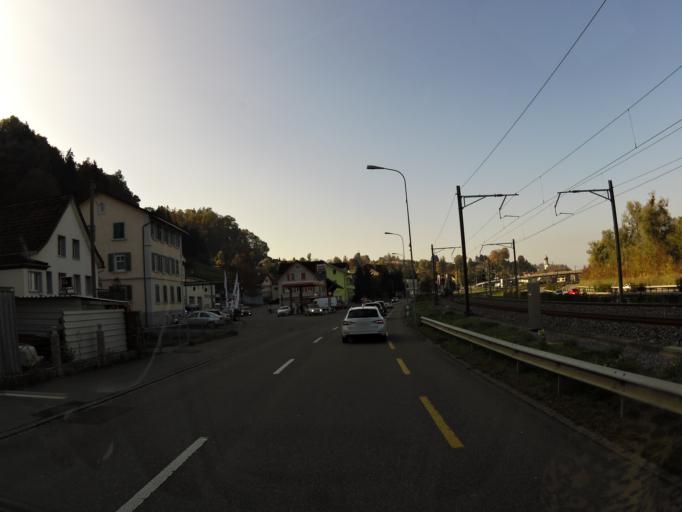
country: AT
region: Vorarlberg
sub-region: Politischer Bezirk Bregenz
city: Gaissau
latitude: 47.4615
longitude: 9.5973
